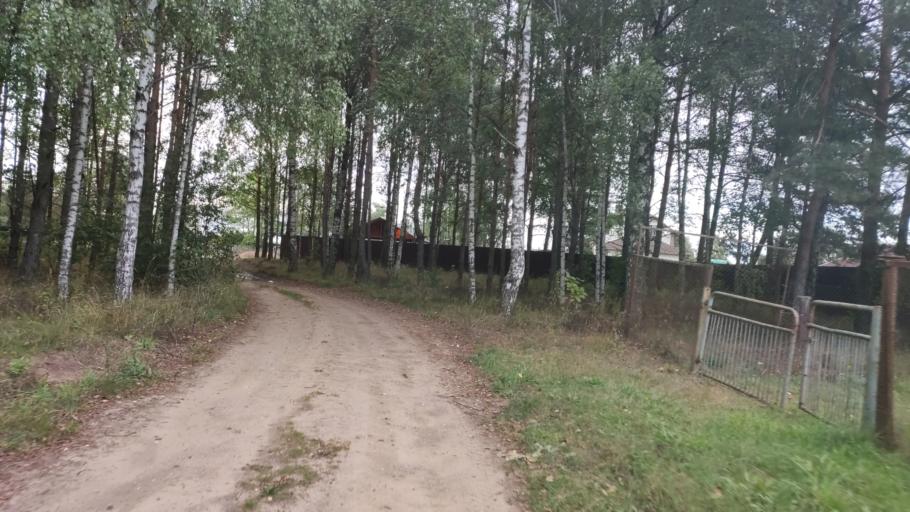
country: BY
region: Minsk
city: Narach
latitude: 54.9287
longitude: 26.6879
